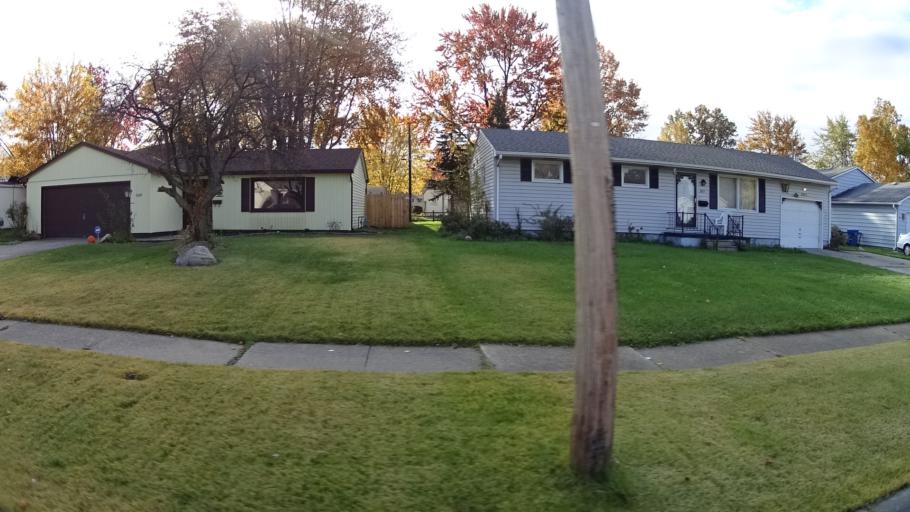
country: US
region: Ohio
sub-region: Lorain County
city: Lorain
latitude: 41.4312
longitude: -82.1961
